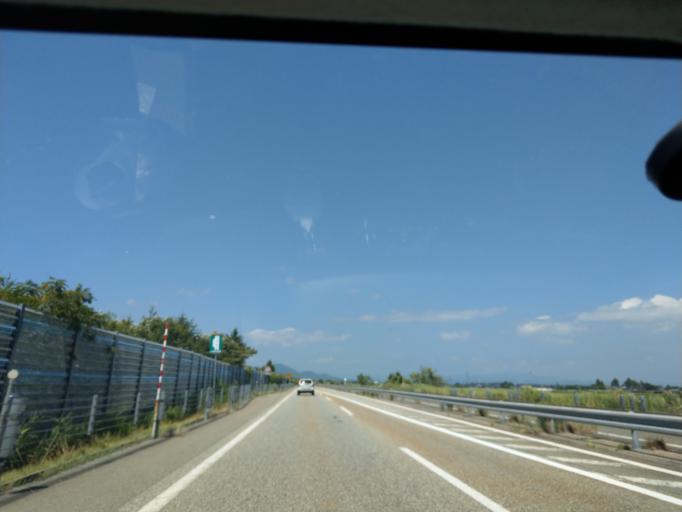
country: JP
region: Akita
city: Omagari
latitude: 39.3706
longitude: 140.4850
